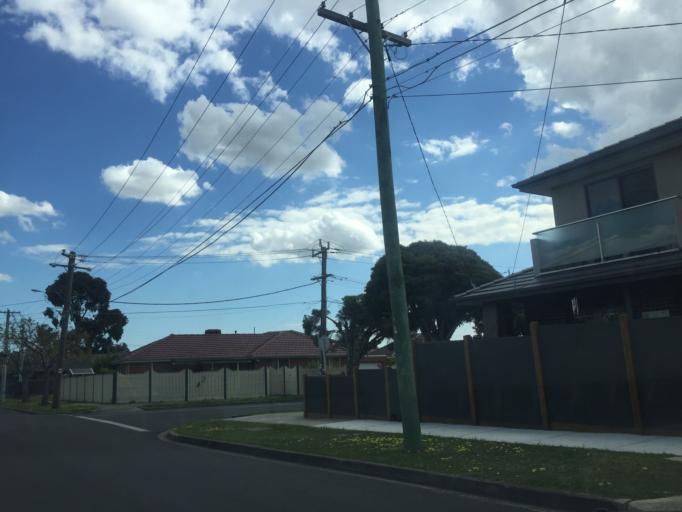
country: AU
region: Victoria
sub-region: Darebin
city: Kingsbury
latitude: -37.7135
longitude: 145.0393
